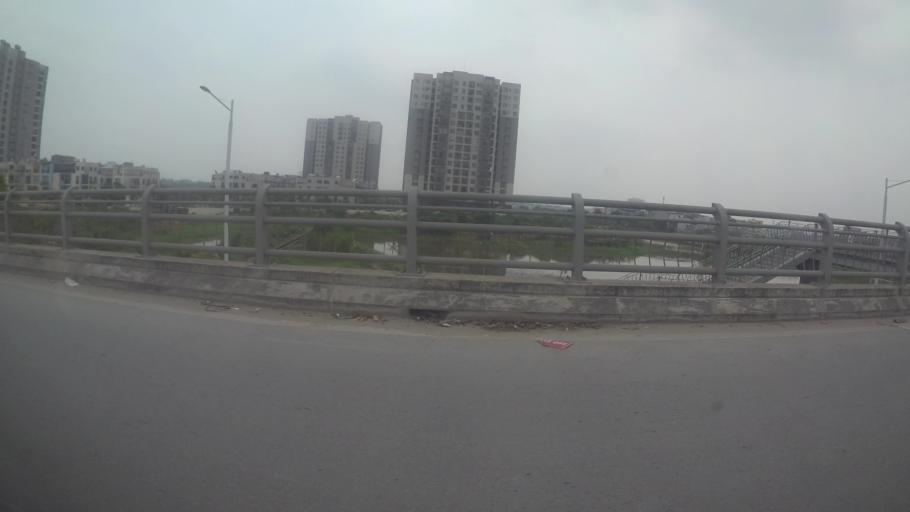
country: VN
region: Ha Noi
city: Cau Dien
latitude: 21.0335
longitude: 105.7534
